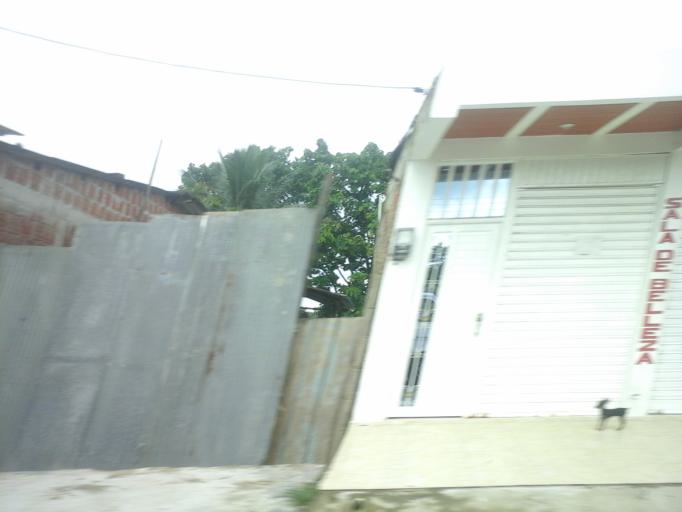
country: CO
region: Putumayo
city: Puerto Asis
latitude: 0.5951
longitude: -76.5669
